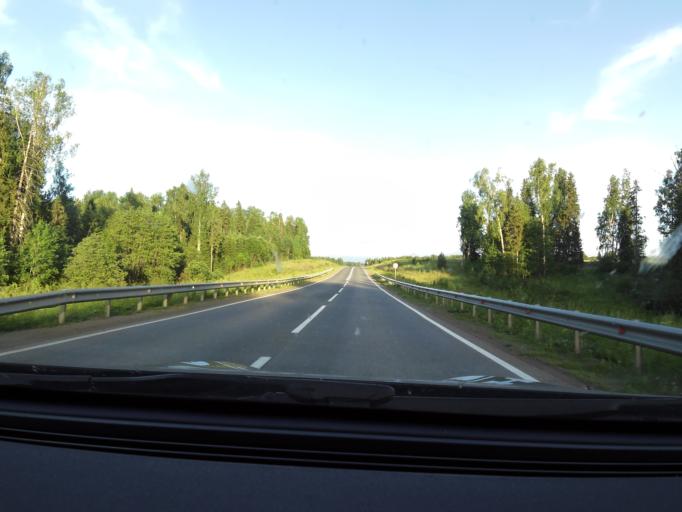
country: RU
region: Perm
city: Siva
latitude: 58.5192
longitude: 54.0093
